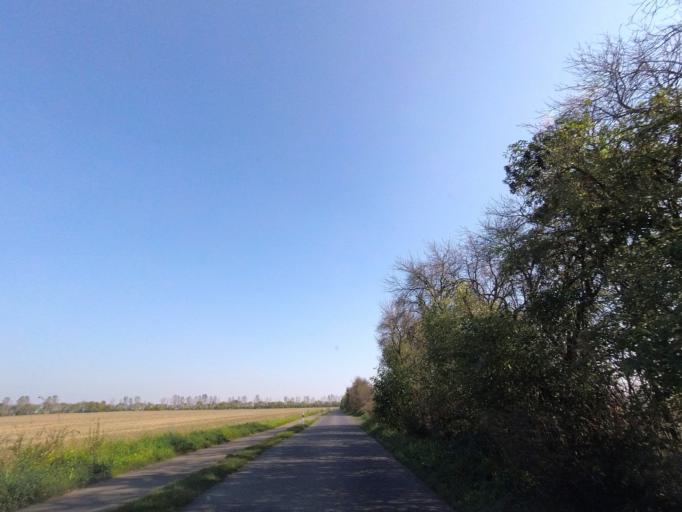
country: DE
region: Brandenburg
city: Niedergorsdorf
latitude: 51.9520
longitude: 12.9851
